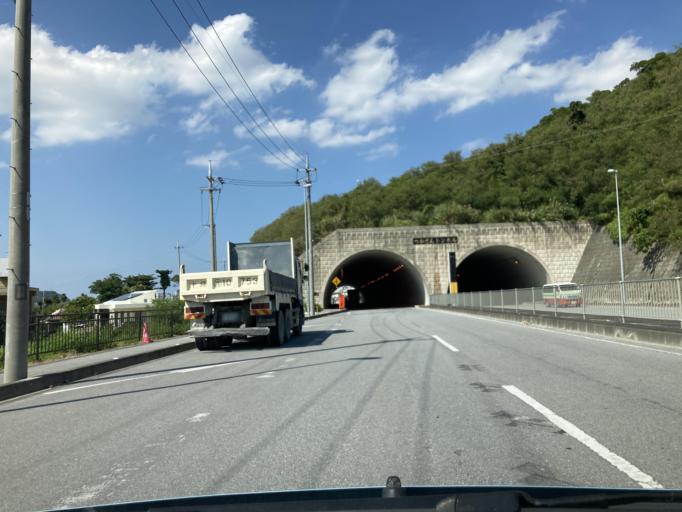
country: JP
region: Okinawa
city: Tomigusuku
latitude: 26.1875
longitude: 127.7195
